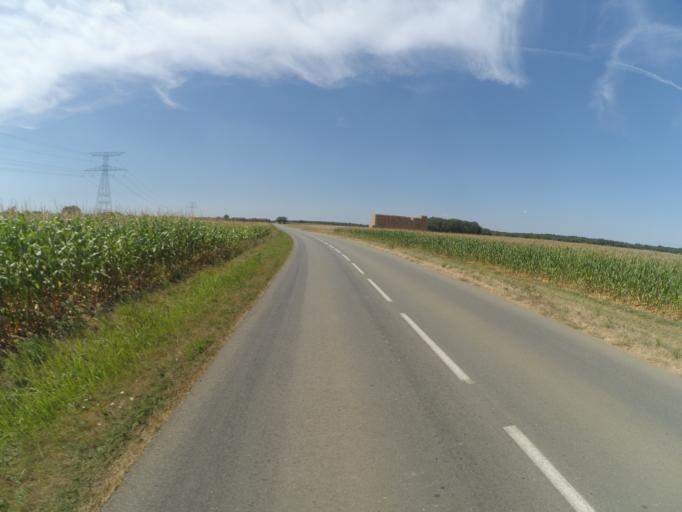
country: FR
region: Poitou-Charentes
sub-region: Departement de la Vienne
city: Saint-Maurice-la-Clouere
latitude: 46.3973
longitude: 0.3709
